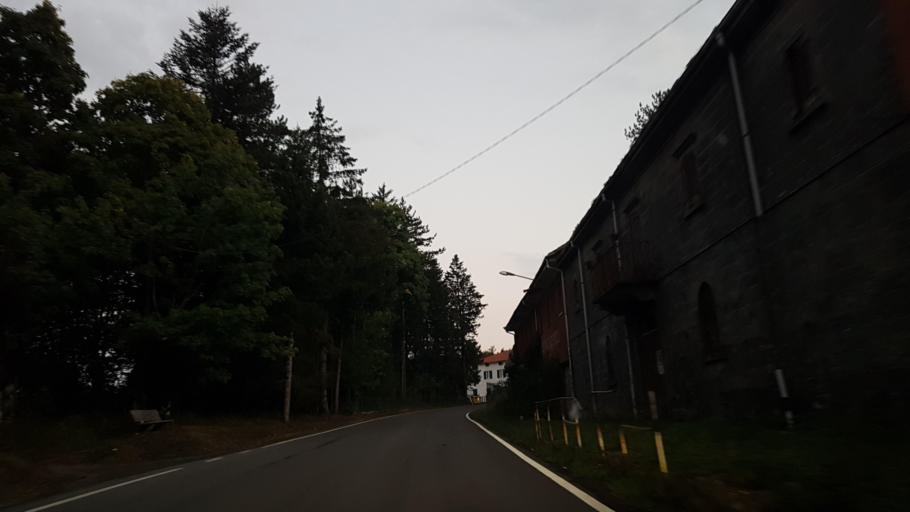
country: IT
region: Liguria
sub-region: Provincia di La Spezia
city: Varese Ligure
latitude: 44.4262
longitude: 9.6222
